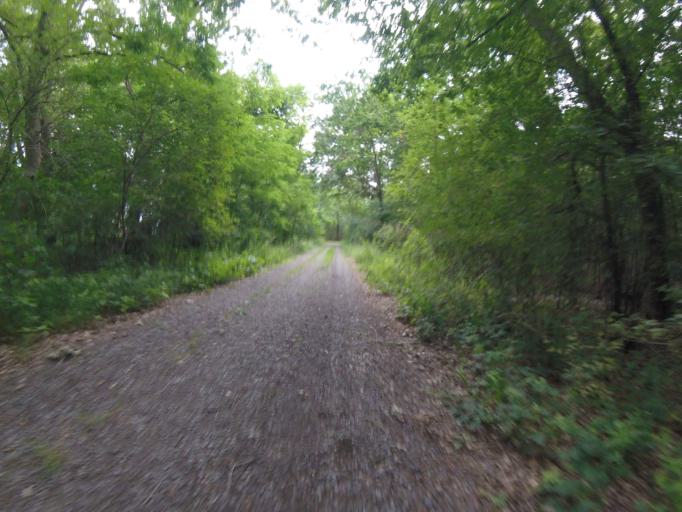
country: DE
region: Brandenburg
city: Gross Koris
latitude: 52.1517
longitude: 13.6744
